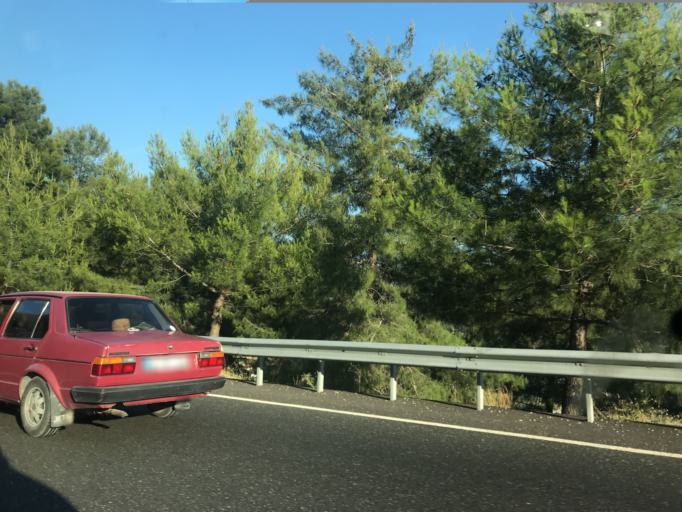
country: TR
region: Mugla
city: Yerkesik
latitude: 37.0597
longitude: 28.3370
